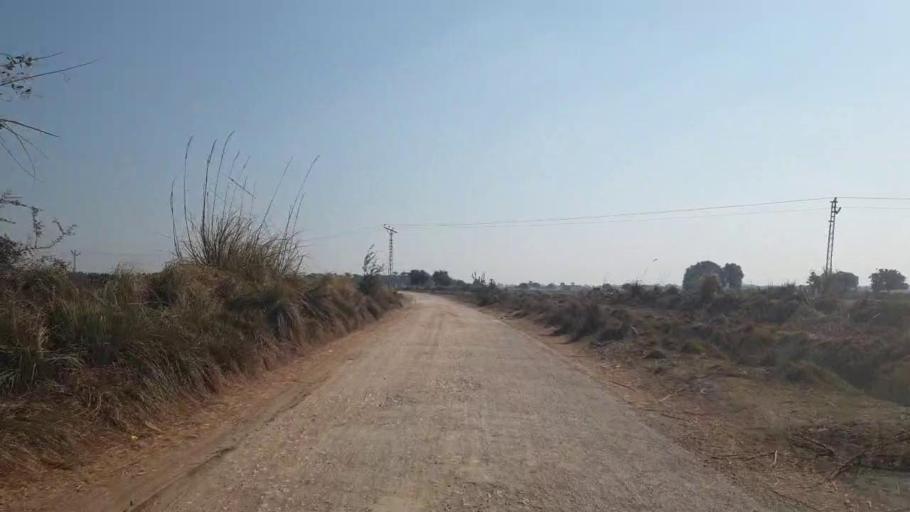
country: PK
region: Sindh
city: Shahdadpur
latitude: 25.9441
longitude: 68.6363
